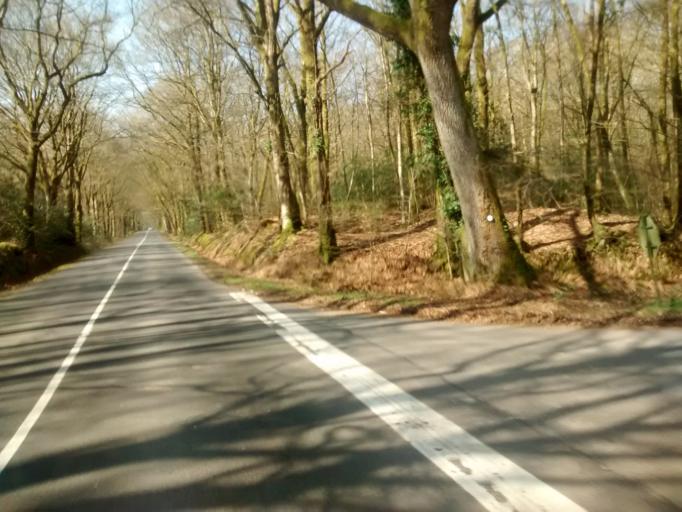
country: FR
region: Brittany
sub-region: Departement d'Ille-et-Vilaine
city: Paimpont
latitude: 48.0181
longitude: -2.1573
